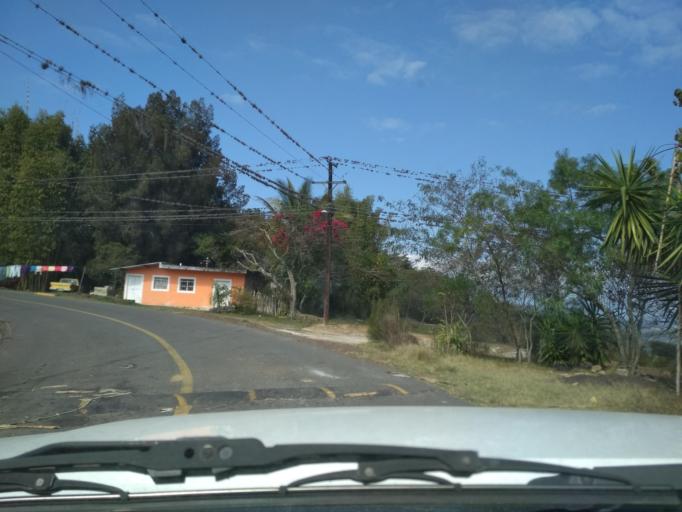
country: MX
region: Veracruz
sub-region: Coatepec
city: Tuzamapan
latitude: 19.3679
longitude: -96.8921
